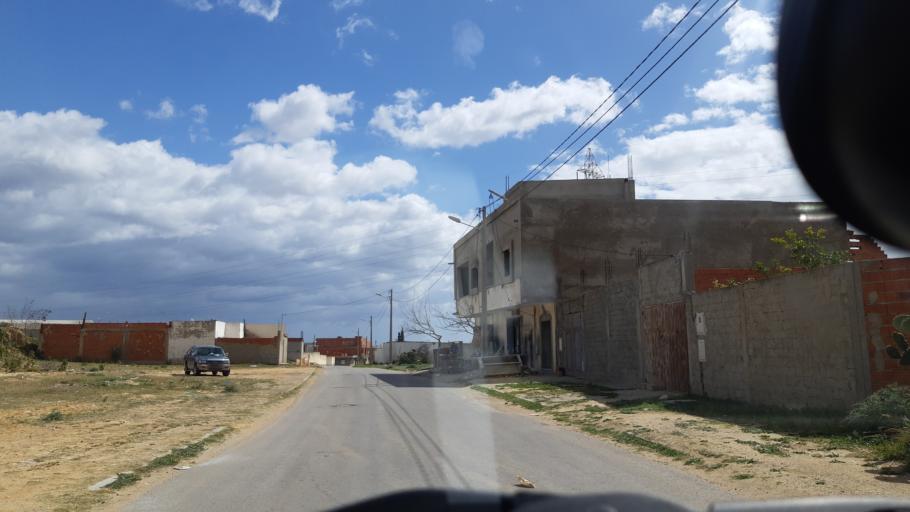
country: TN
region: Susah
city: Akouda
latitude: 35.8788
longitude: 10.5131
